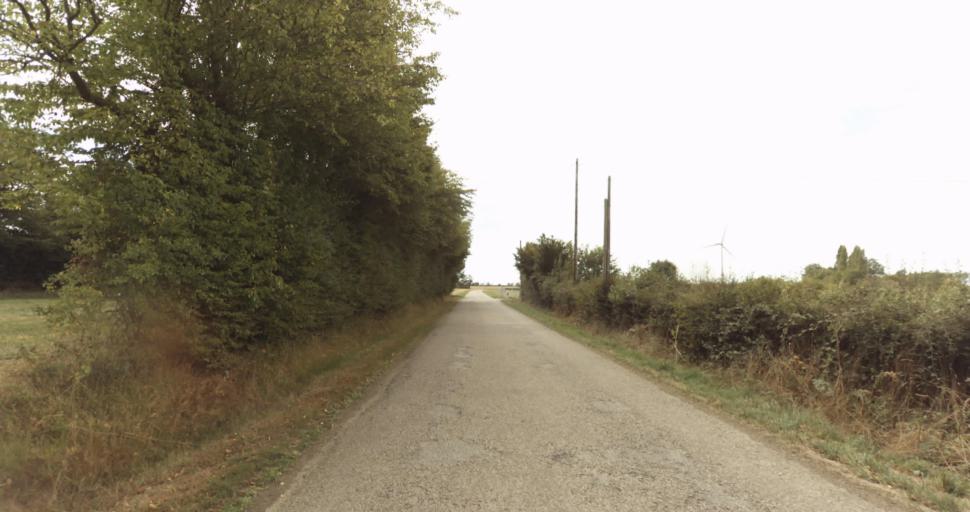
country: FR
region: Lower Normandy
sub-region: Departement du Calvados
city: La Vespiere
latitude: 48.9690
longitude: 0.3747
